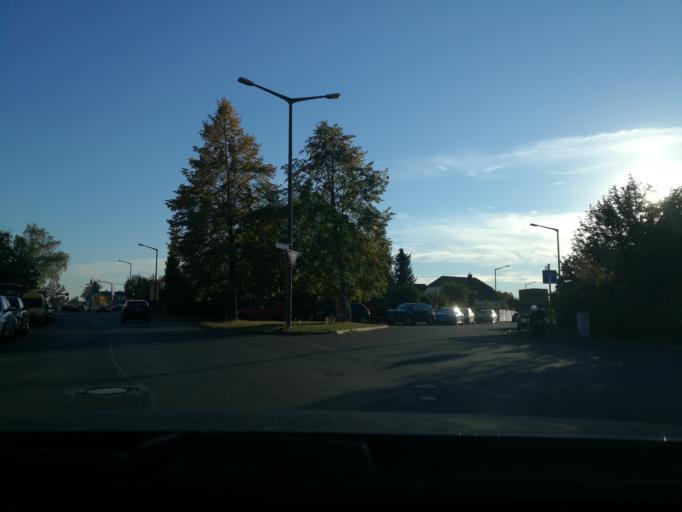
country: DE
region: Bavaria
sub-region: Regierungsbezirk Mittelfranken
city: Furth
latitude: 49.5244
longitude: 11.0076
